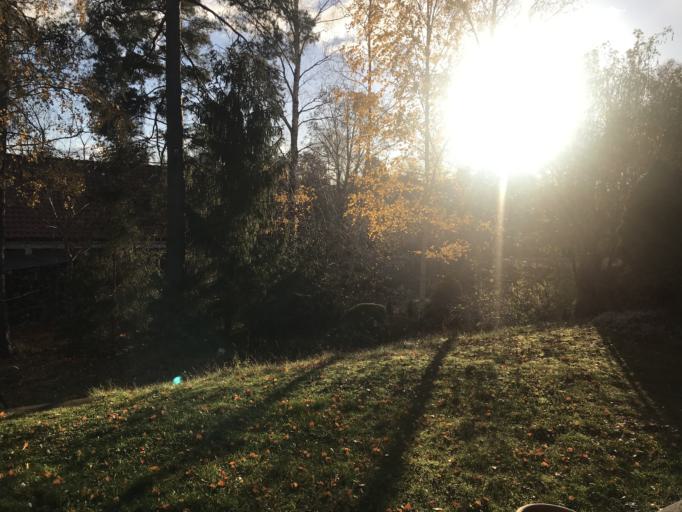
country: SE
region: Stockholm
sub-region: Taby Kommun
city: Taby
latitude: 59.4386
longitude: 18.0926
